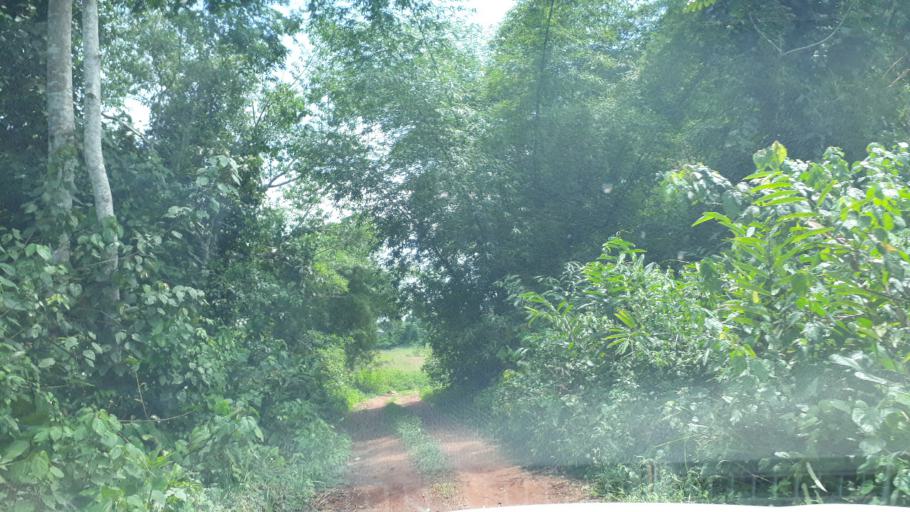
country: CD
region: Eastern Province
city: Kisangani
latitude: 0.4784
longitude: 25.5125
